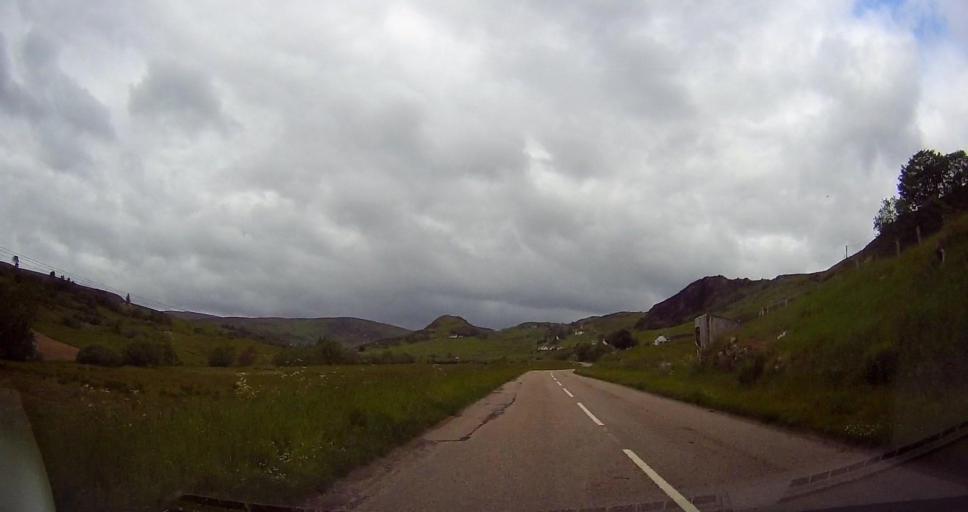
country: GB
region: Scotland
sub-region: Highland
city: Dornoch
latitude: 58.0052
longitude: -4.2331
